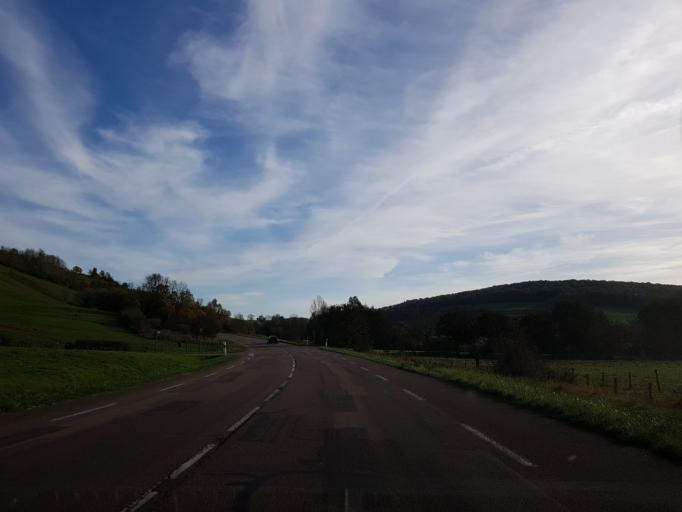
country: FR
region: Bourgogne
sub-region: Departement de la Cote-d'Or
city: Vitteaux
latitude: 47.3659
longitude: 4.5654
